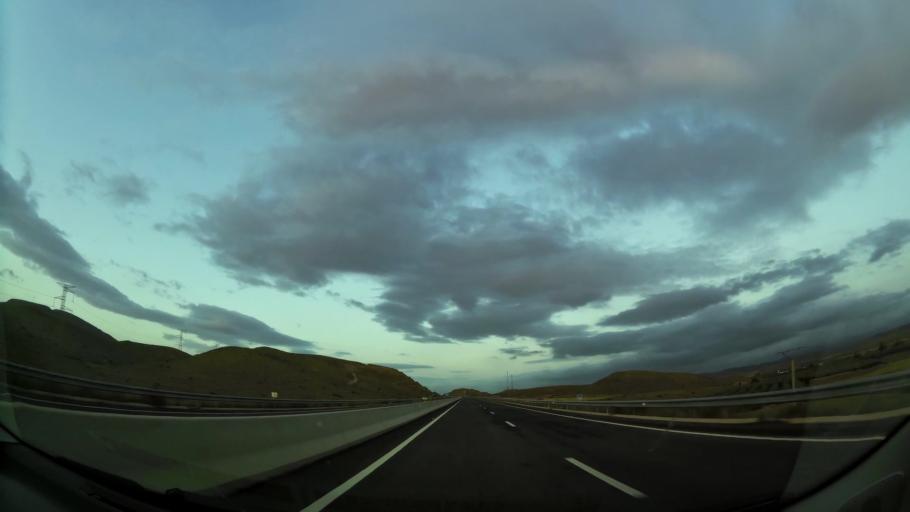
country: MA
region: Oriental
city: El Aioun
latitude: 34.5948
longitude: -2.6729
